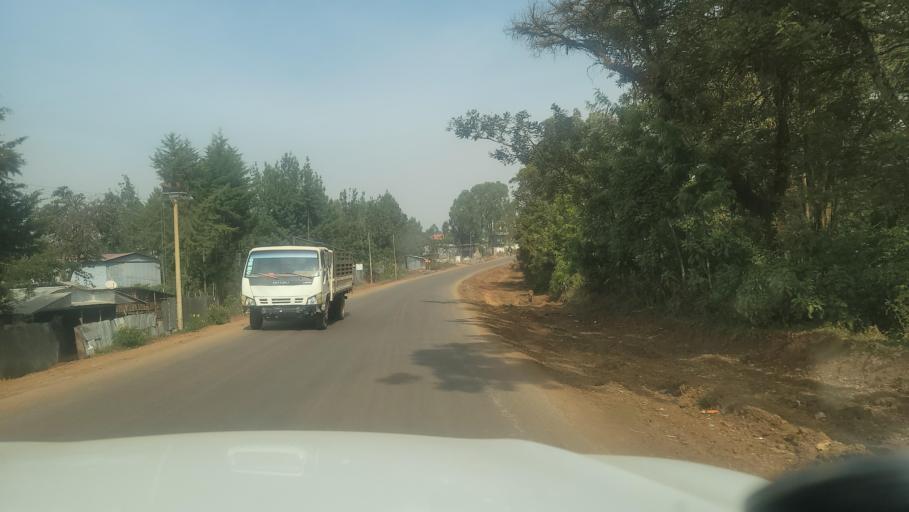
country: ET
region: Oromiya
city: Jima
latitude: 7.7028
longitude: 36.8061
